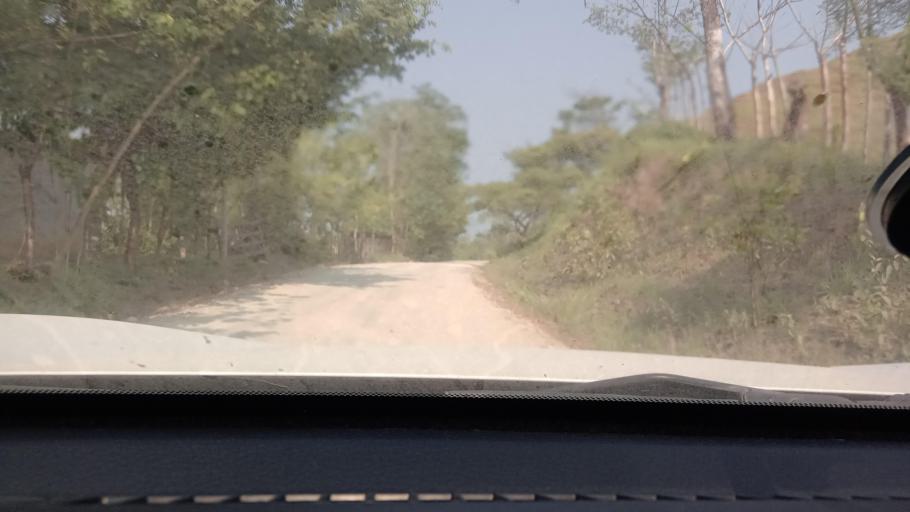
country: MX
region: Tabasco
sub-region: Huimanguillo
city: Francisco Rueda
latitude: 17.6204
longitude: -93.9476
